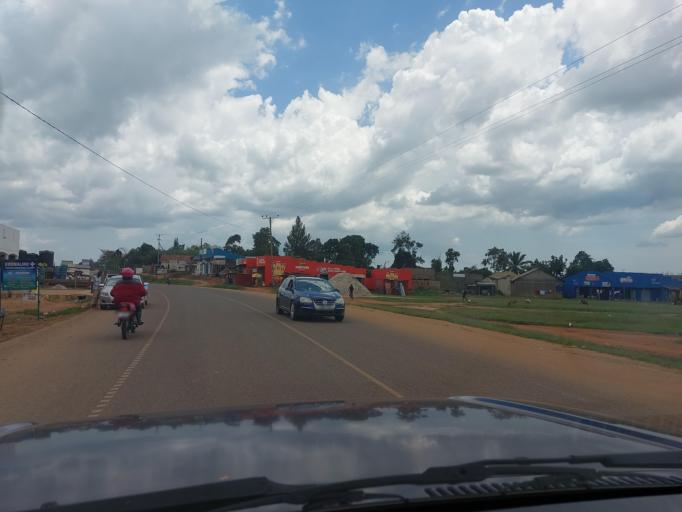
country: UG
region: Central Region
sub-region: Mukono District
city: Mukono
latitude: 0.3165
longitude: 32.7698
